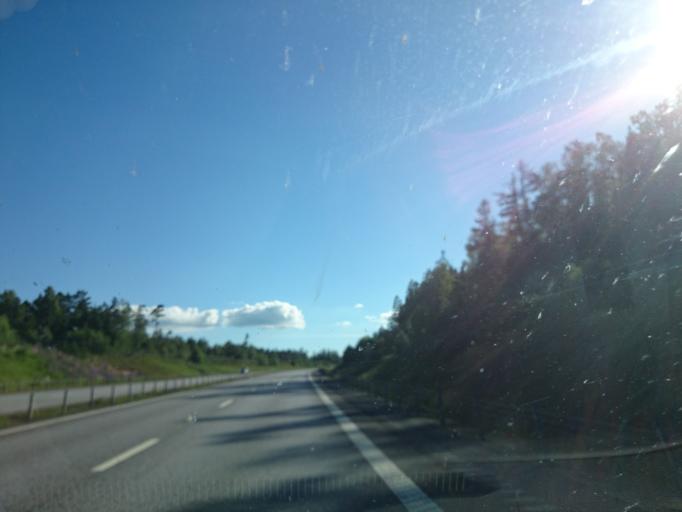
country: SE
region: Skane
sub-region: Orkelljunga Kommun
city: OErkelljunga
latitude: 56.3285
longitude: 13.4449
